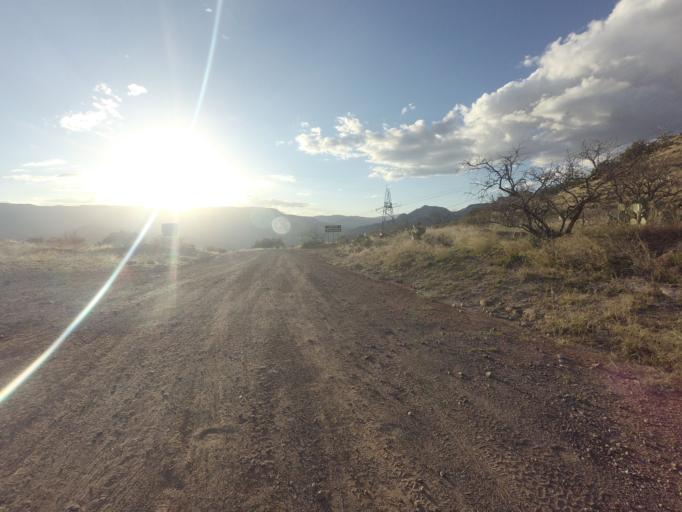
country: US
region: Arizona
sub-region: Gila County
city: Pine
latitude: 34.3596
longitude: -111.6783
